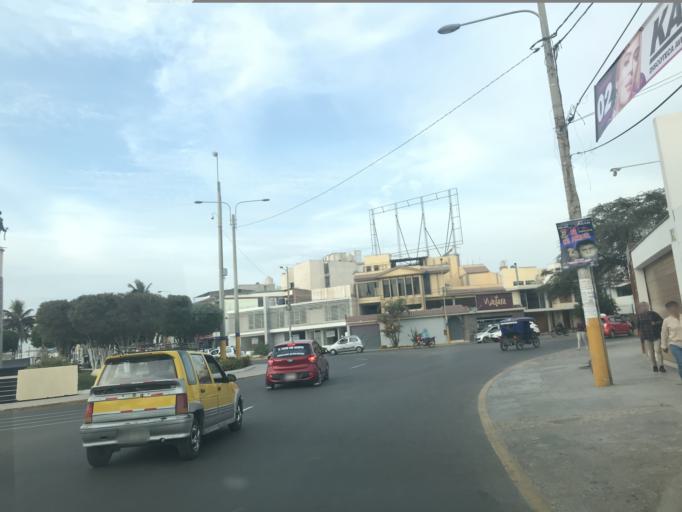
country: PE
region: Lambayeque
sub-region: Provincia de Chiclayo
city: Chiclayo
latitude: -6.7824
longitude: -79.8428
